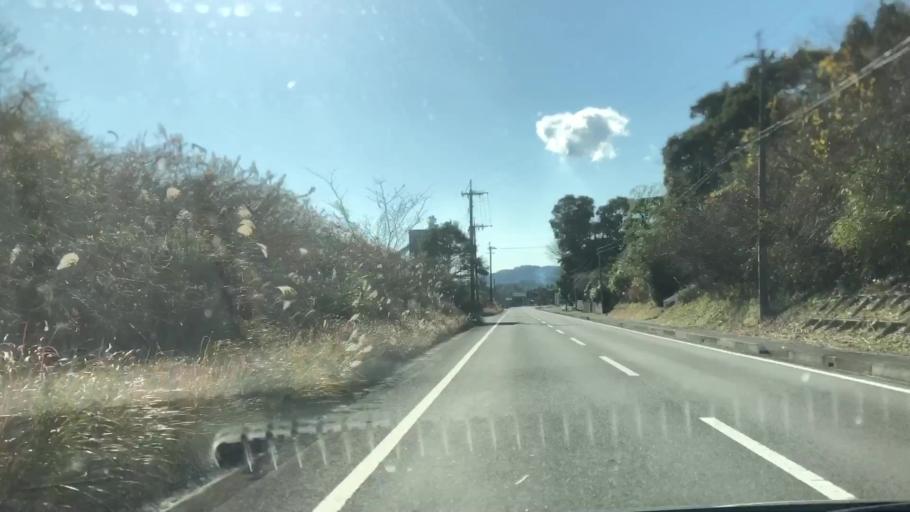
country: JP
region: Kagoshima
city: Satsumasendai
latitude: 31.8619
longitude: 130.4166
